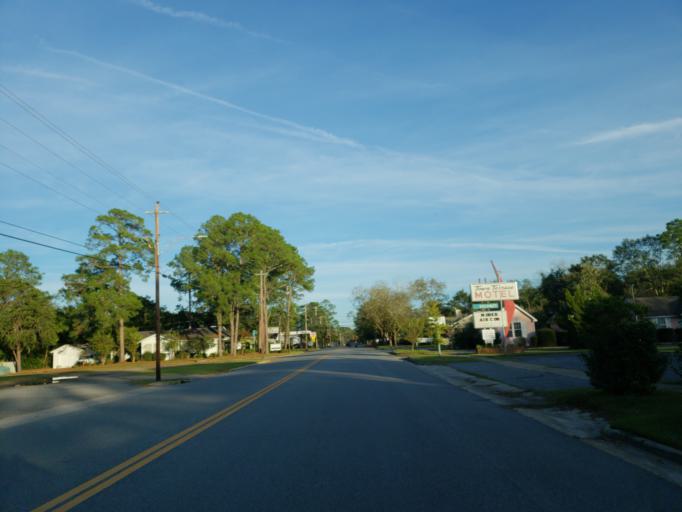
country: US
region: Georgia
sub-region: Tift County
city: Tifton
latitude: 31.4648
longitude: -83.5108
